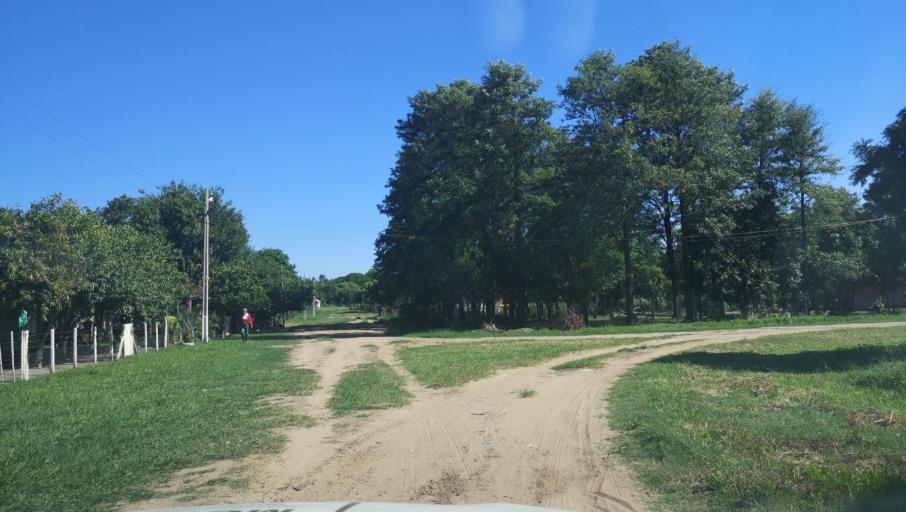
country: PY
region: Caaguazu
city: Carayao
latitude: -25.2054
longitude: -56.3959
